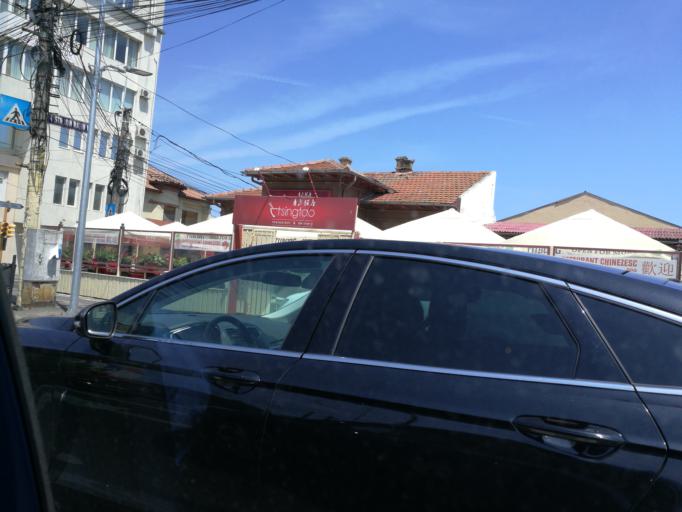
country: RO
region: Constanta
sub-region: Municipiul Constanta
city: Constanta
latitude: 44.1967
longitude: 28.6485
